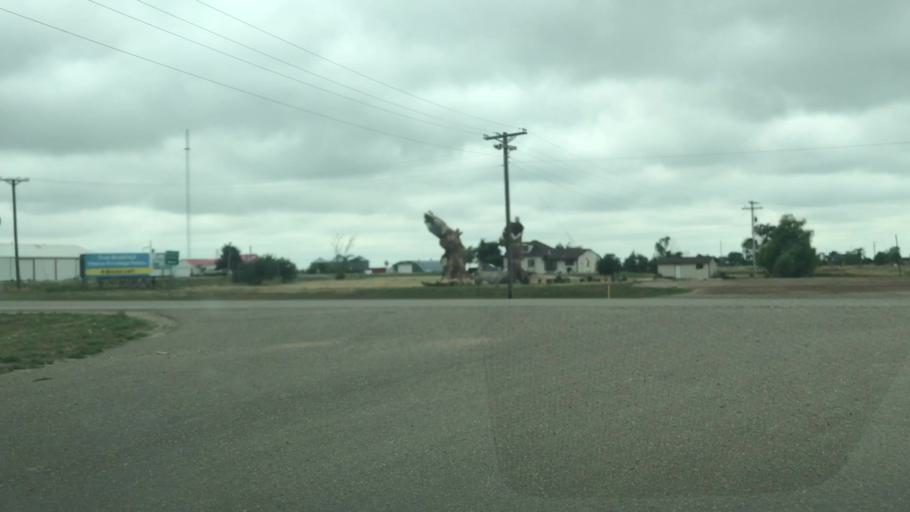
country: US
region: South Dakota
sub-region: Jackson County
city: Kadoka
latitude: 43.8368
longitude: -101.5222
